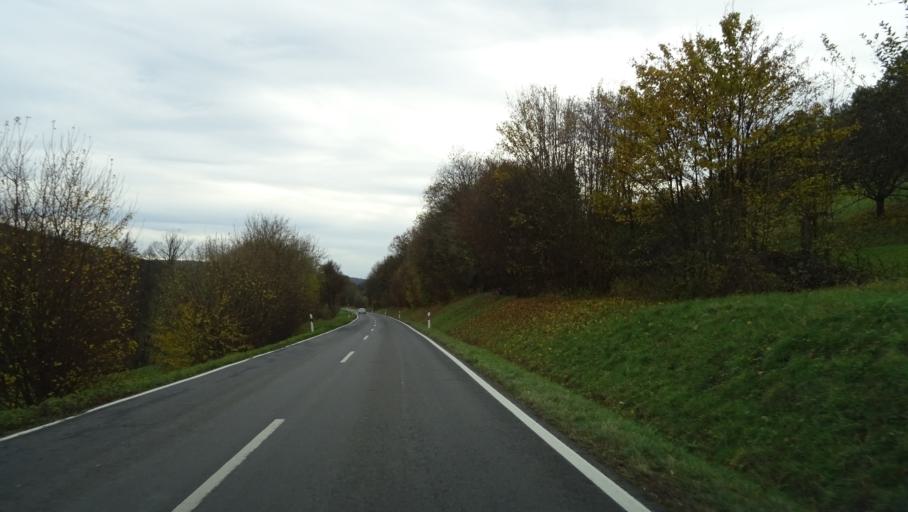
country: DE
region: Baden-Wuerttemberg
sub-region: Karlsruhe Region
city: Mosbach
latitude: 49.3663
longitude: 9.1263
